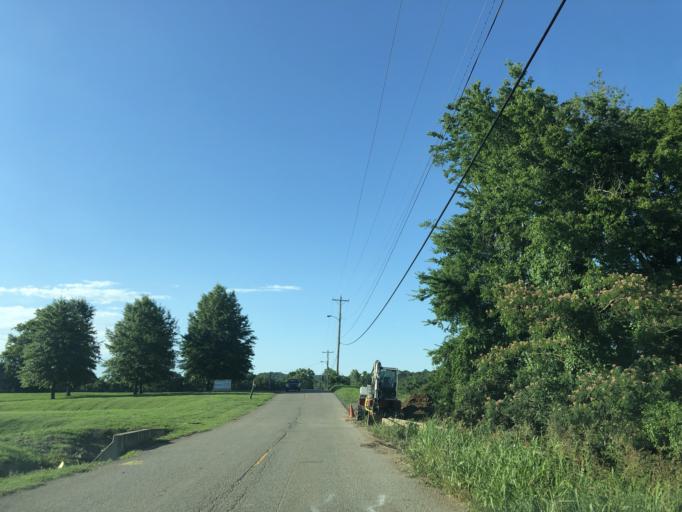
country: US
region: Tennessee
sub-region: Davidson County
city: Nashville
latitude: 36.2018
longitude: -86.8614
